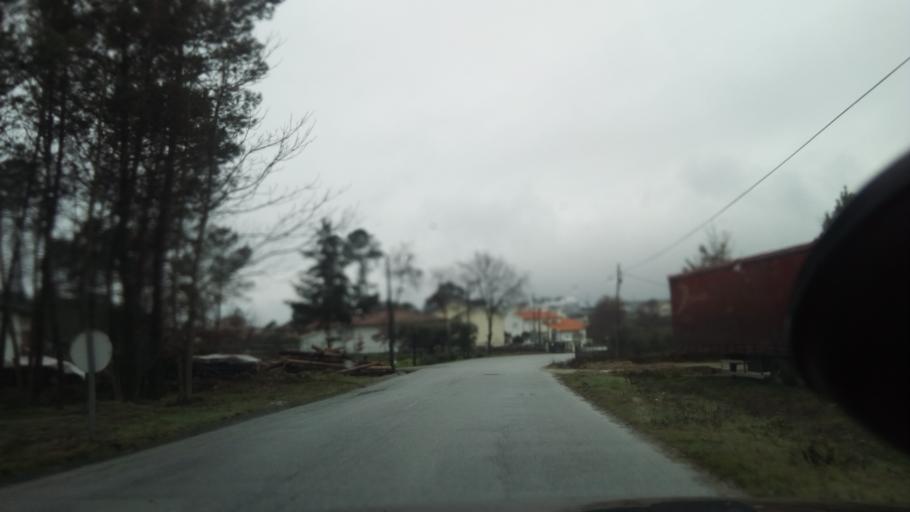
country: PT
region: Viseu
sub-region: Mangualde
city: Mangualde
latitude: 40.6165
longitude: -7.7934
